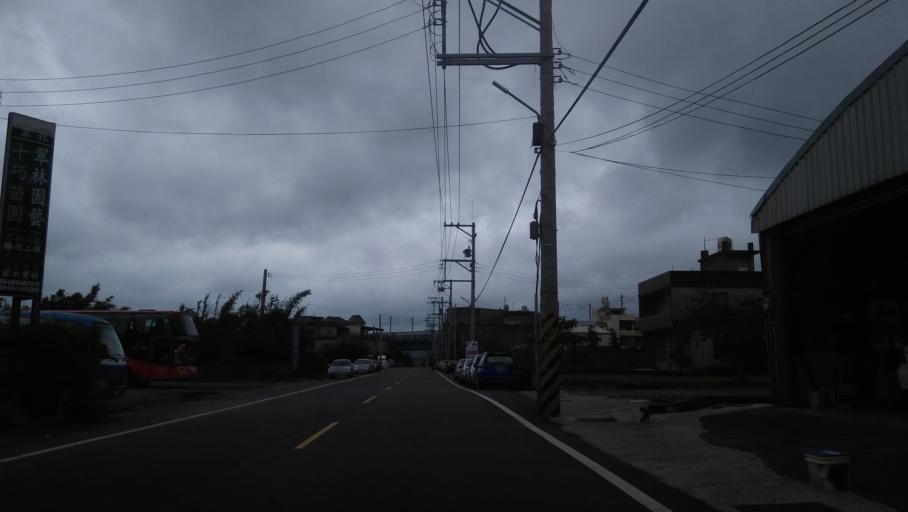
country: TW
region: Taiwan
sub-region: Hsinchu
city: Zhubei
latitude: 24.7820
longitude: 121.0320
